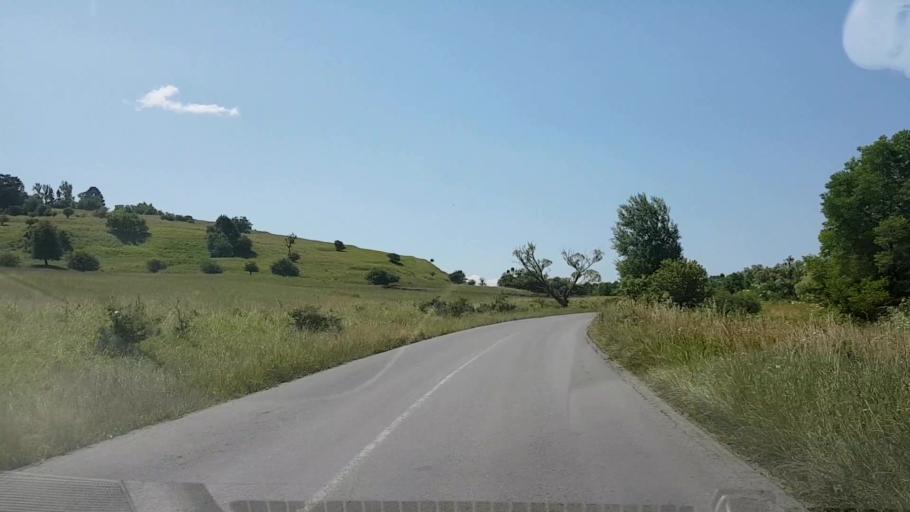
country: RO
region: Brasov
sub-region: Comuna Cincu
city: Cincu
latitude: 45.9513
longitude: 24.7843
